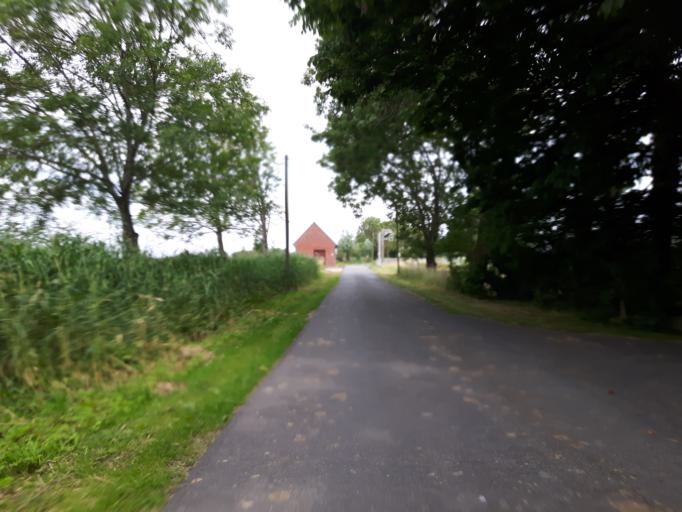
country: DE
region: Lower Saxony
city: Varel
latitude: 53.3613
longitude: 8.2051
